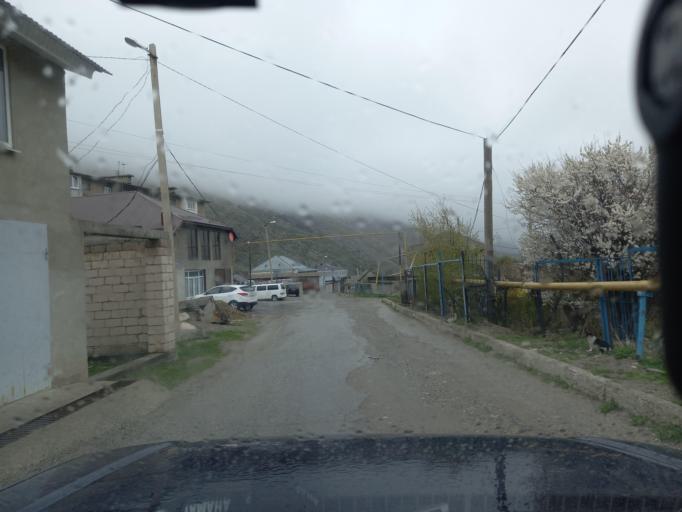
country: RU
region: Kabardino-Balkariya
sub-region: El'brusskiy Rayon
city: El'brus
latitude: 43.2590
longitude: 42.6465
